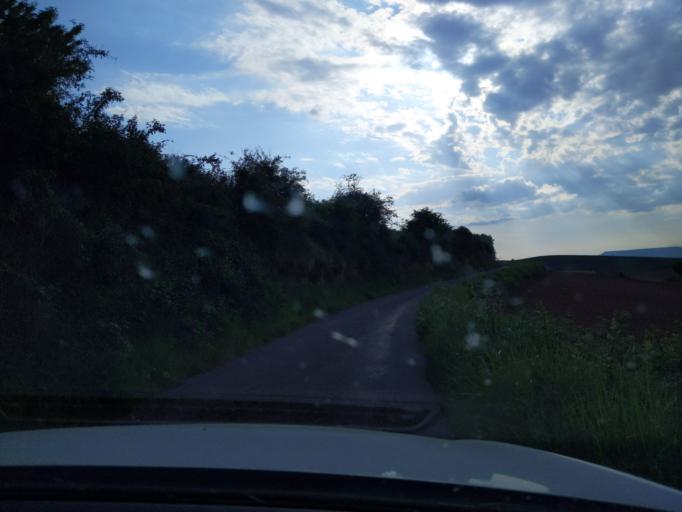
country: ES
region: La Rioja
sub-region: Provincia de La Rioja
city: Clavijo
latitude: 42.3543
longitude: -2.4372
